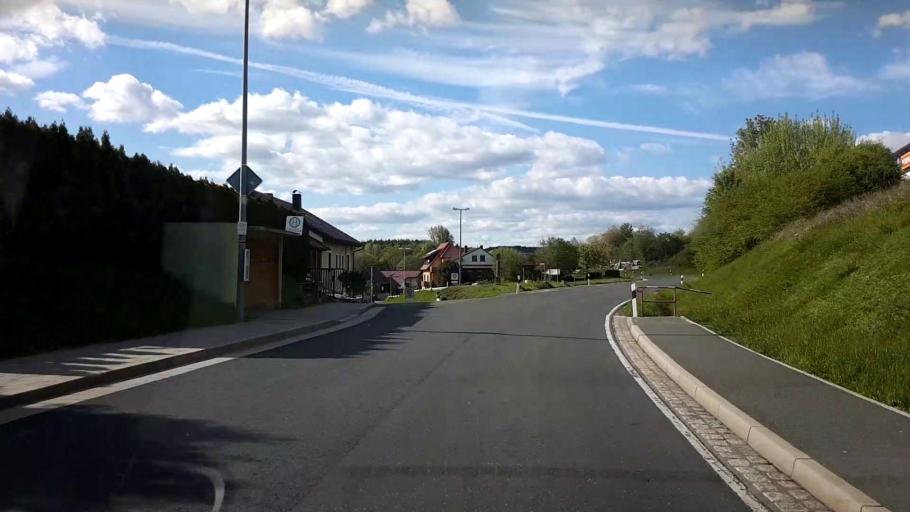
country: DE
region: Bavaria
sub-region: Upper Franconia
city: Hollfeld
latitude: 49.9412
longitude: 11.2837
